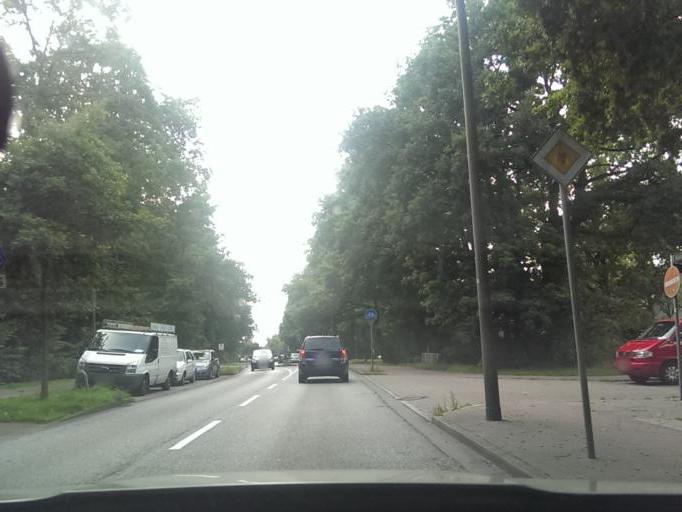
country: DE
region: Hamburg
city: Langenhorn
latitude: 53.6488
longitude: 9.9937
